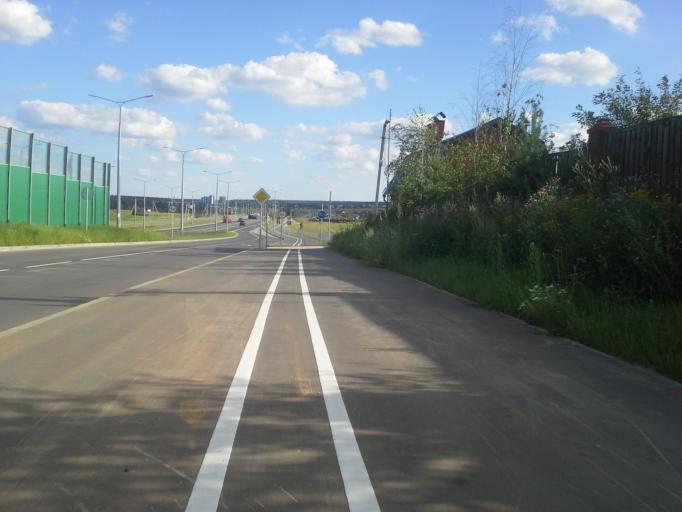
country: RU
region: Moskovskaya
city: Annino
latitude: 55.5265
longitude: 37.2372
